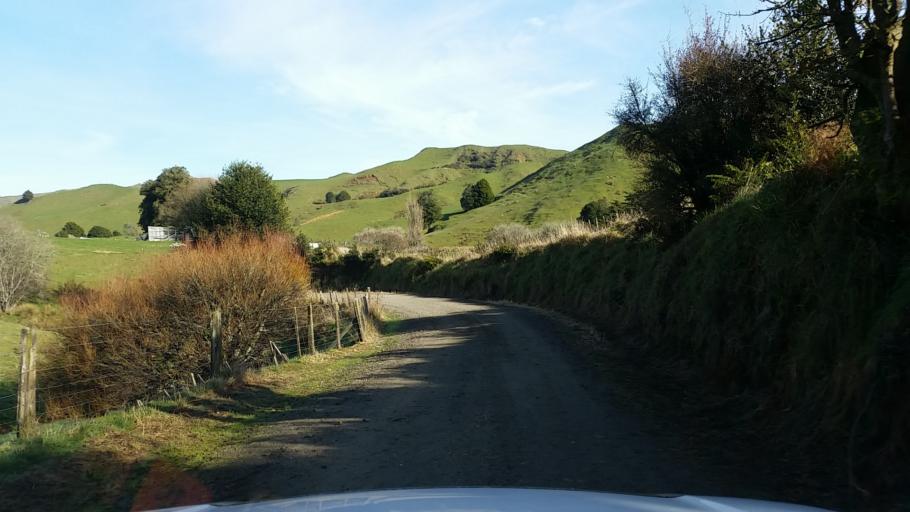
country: NZ
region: Taranaki
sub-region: South Taranaki District
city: Eltham
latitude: -39.3112
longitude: 174.5400
